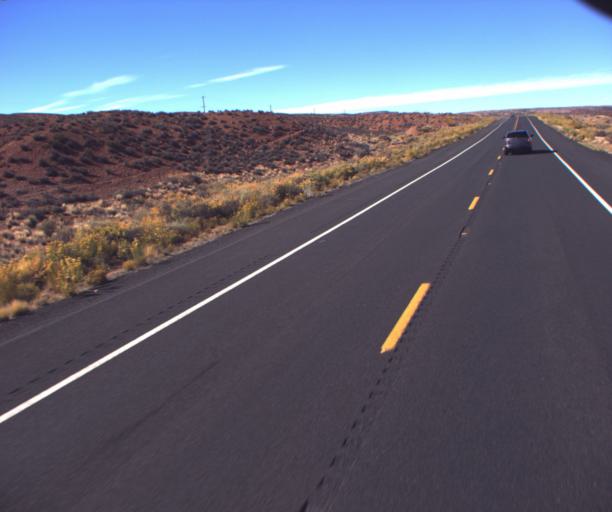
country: US
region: Arizona
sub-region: Coconino County
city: Tuba City
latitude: 36.3104
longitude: -111.4676
